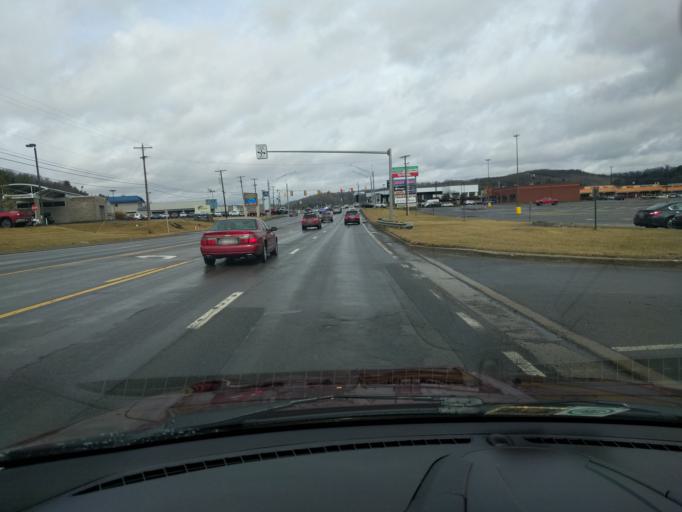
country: US
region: West Virginia
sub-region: Raleigh County
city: Beckley
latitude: 37.8012
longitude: -81.1848
